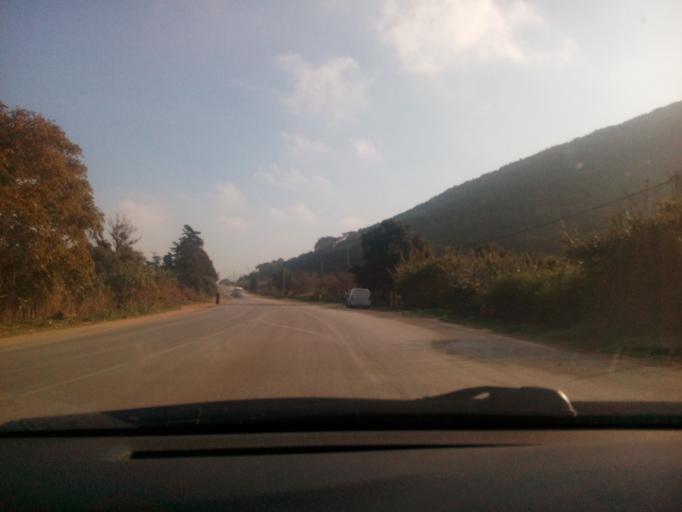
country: DZ
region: Oran
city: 'Ain el Turk
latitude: 35.7039
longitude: -0.8374
